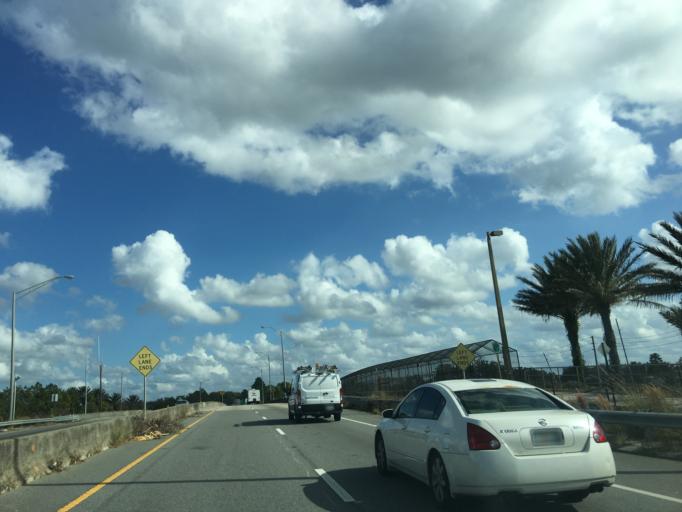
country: US
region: Florida
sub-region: Orange County
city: Maitland
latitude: 28.6370
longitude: -81.3611
